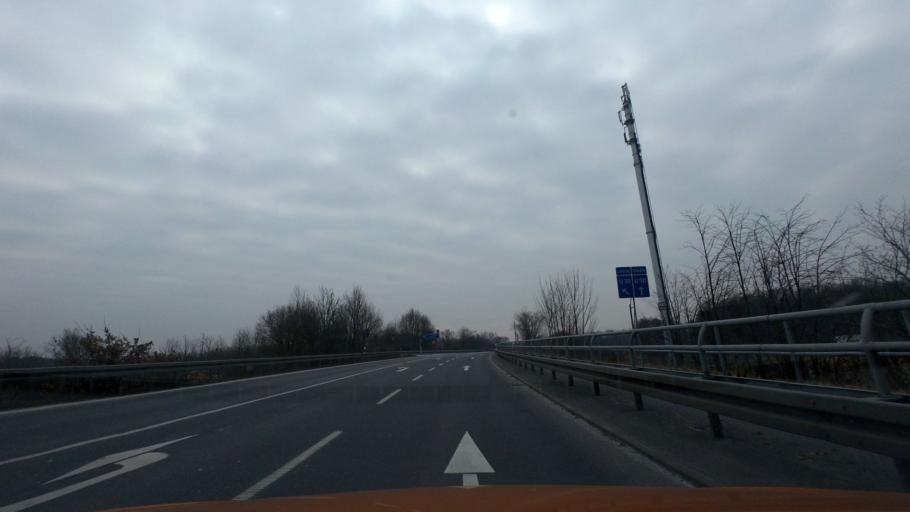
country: DE
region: Brandenburg
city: Ludwigsfelde
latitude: 52.3031
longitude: 13.2078
